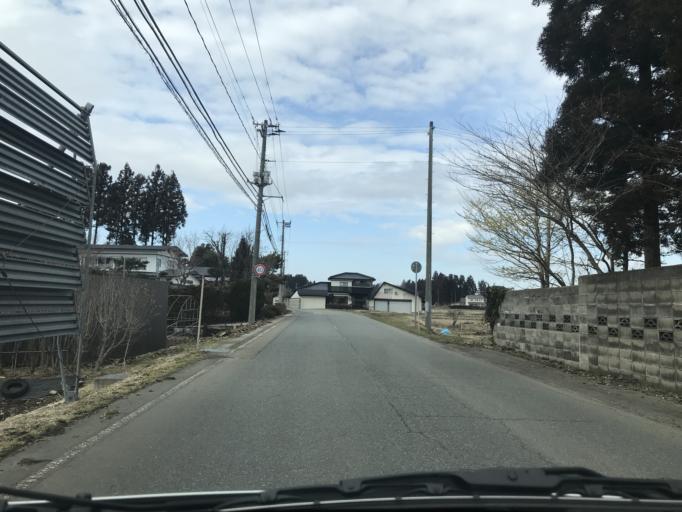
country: JP
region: Iwate
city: Kitakami
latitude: 39.3238
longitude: 140.9858
